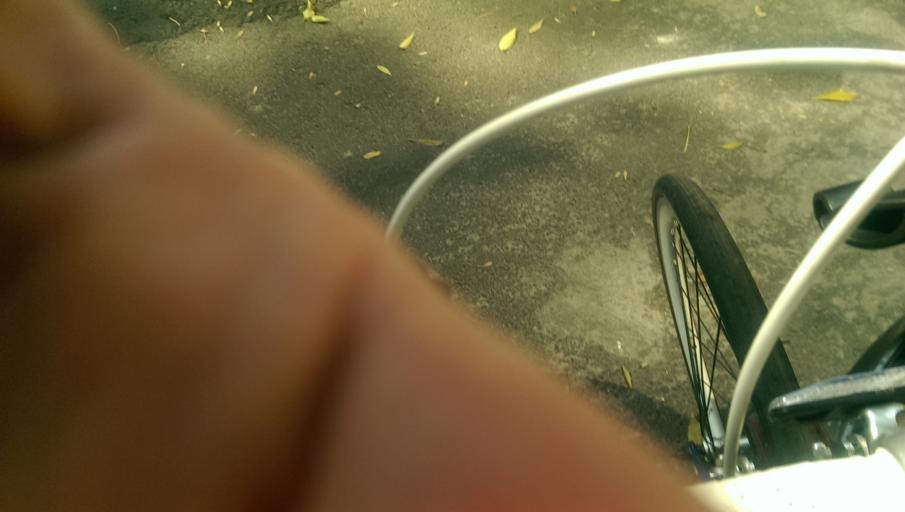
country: MX
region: Mexico City
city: Coyoacan
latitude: 19.3580
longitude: -99.1702
